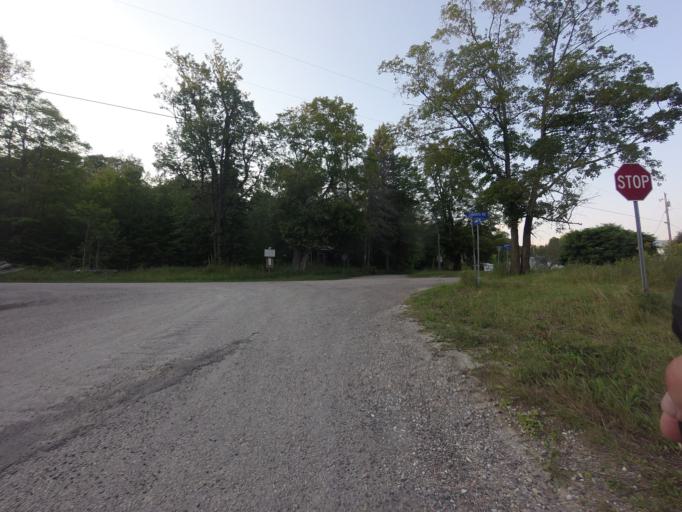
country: CA
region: Ontario
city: Renfrew
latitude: 45.0672
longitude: -76.7616
